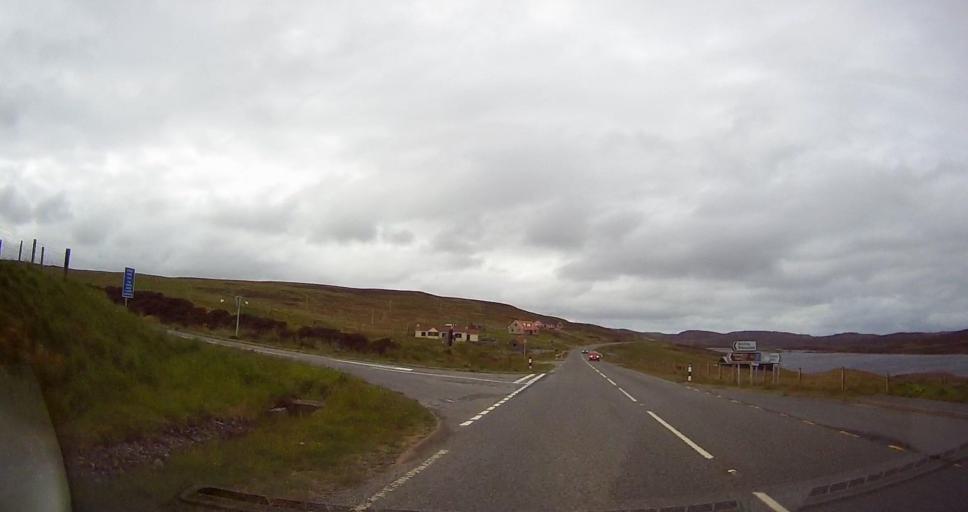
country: GB
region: Scotland
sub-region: Shetland Islands
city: Lerwick
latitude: 60.2543
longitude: -1.4574
